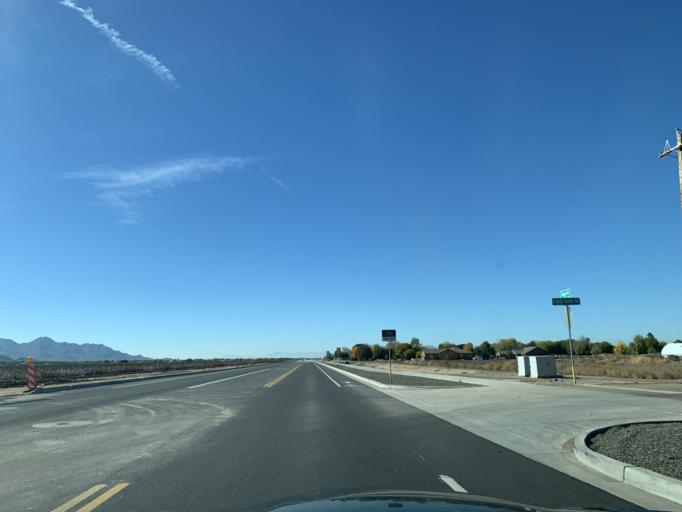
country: US
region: Arizona
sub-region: Maricopa County
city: Queen Creek
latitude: 33.2195
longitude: -111.5998
